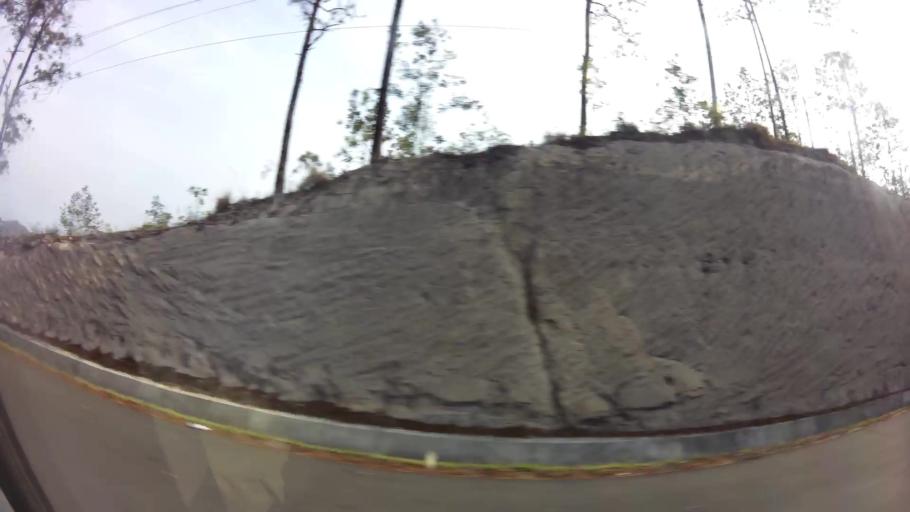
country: HN
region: Francisco Morazan
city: Zambrano
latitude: 14.2846
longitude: -87.4623
